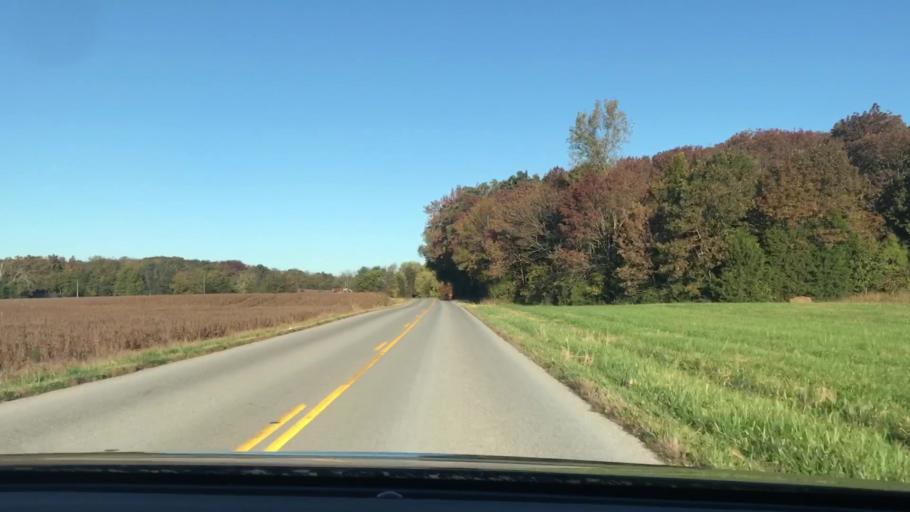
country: US
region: Kentucky
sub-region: Logan County
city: Auburn
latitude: 36.8169
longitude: -86.6437
